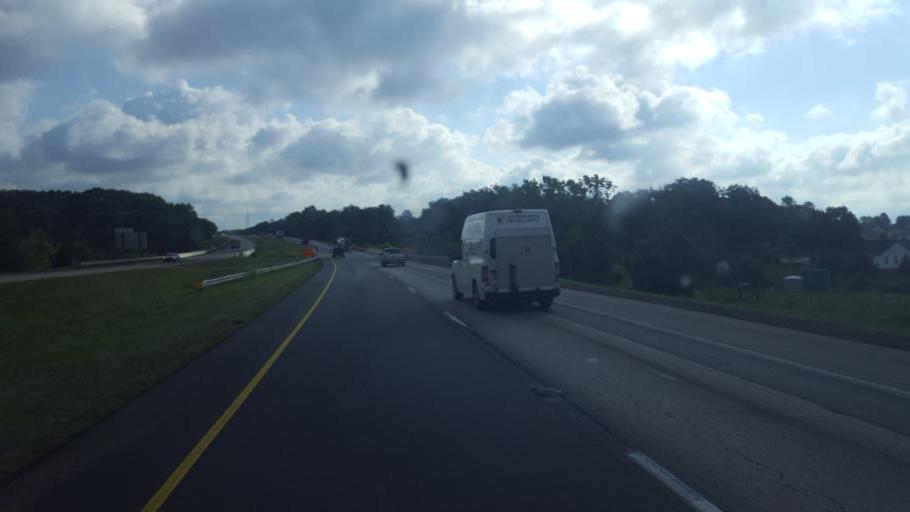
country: US
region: Ohio
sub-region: Stark County
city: Genoa
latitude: 40.7666
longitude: -81.4683
